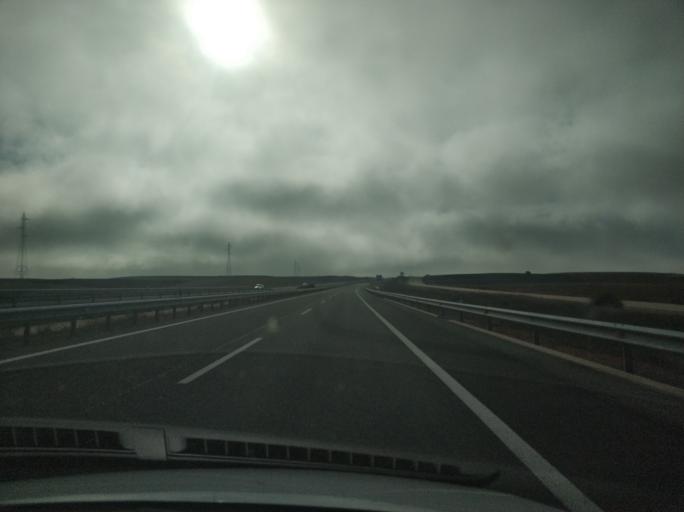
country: ES
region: Castille and Leon
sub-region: Provincia de Soria
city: Alcubilla de las Penas
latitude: 41.2794
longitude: -2.4755
